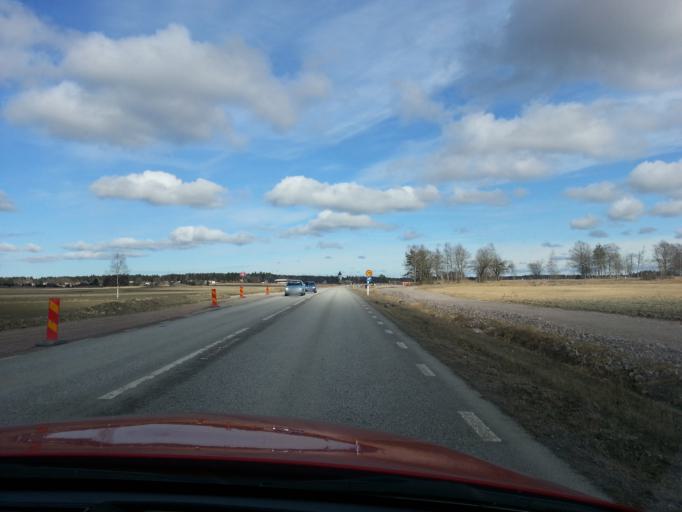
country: SE
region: Uppsala
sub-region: Osthammars Kommun
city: Gimo
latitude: 60.0493
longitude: 18.0505
